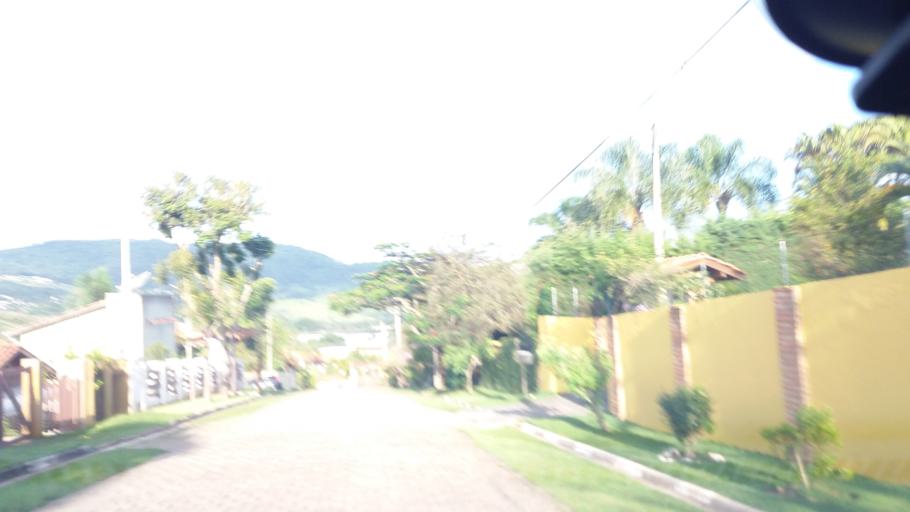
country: BR
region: Sao Paulo
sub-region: Bom Jesus Dos Perdoes
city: Bom Jesus dos Perdoes
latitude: -23.1668
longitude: -46.4559
